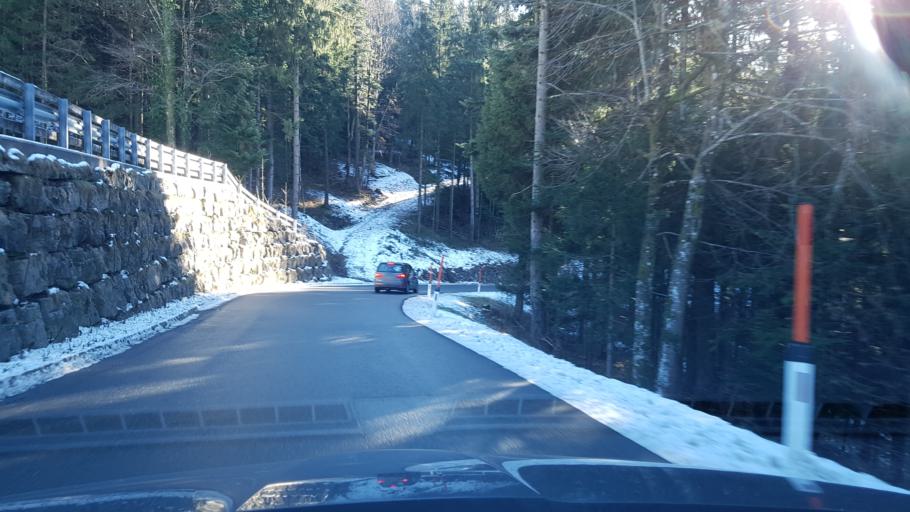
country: AT
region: Salzburg
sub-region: Politischer Bezirk Hallein
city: Golling an der Salzach
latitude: 47.6248
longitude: 13.1867
